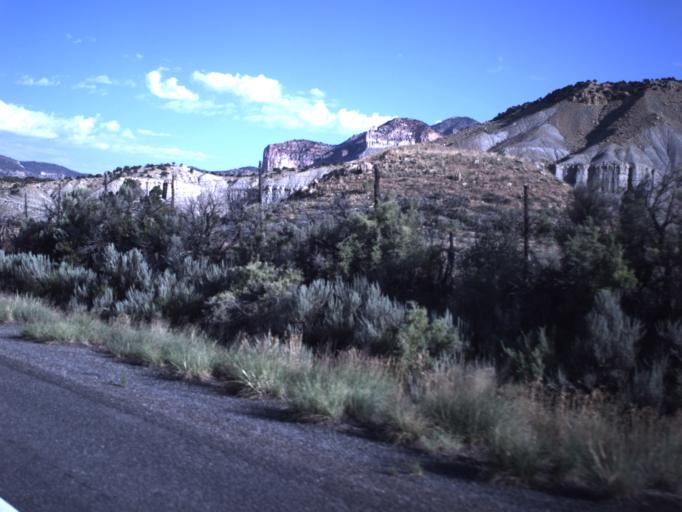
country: US
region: Utah
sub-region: Emery County
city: Huntington
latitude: 39.3621
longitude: -111.0362
